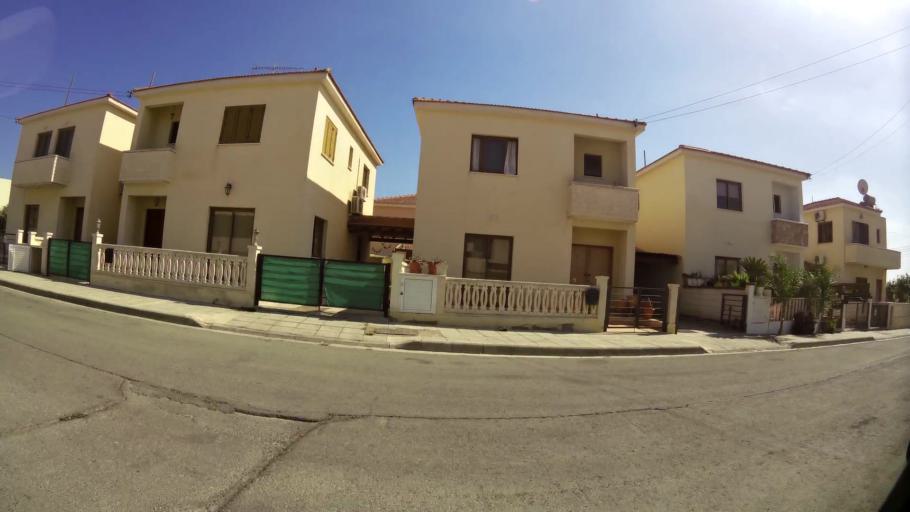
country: CY
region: Larnaka
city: Livadia
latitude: 34.9504
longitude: 33.6176
